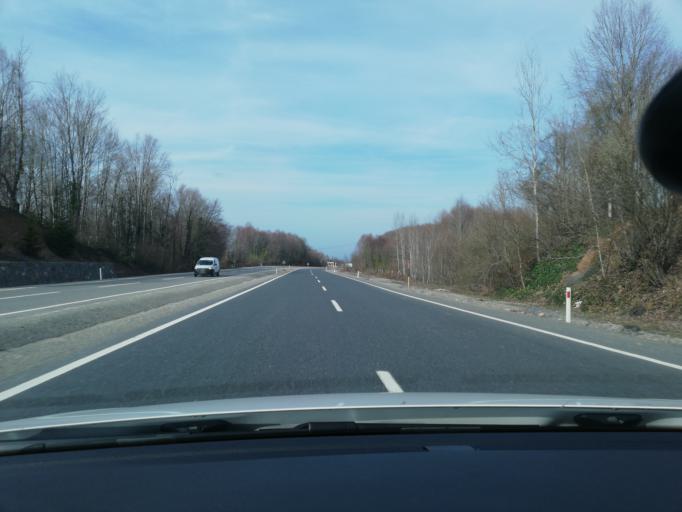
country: TR
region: Zonguldak
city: Kozlu
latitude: 41.3347
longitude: 31.6279
